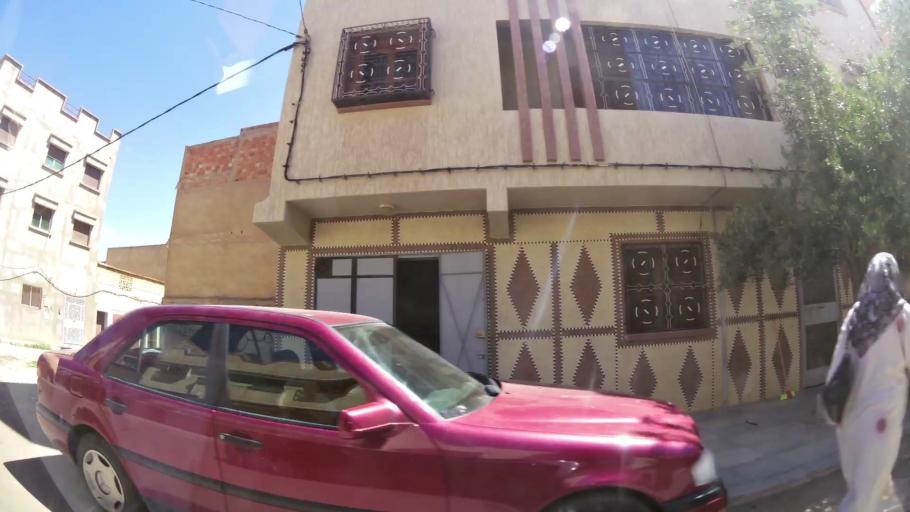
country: MA
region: Oriental
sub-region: Oujda-Angad
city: Oujda
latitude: 34.6672
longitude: -1.9338
